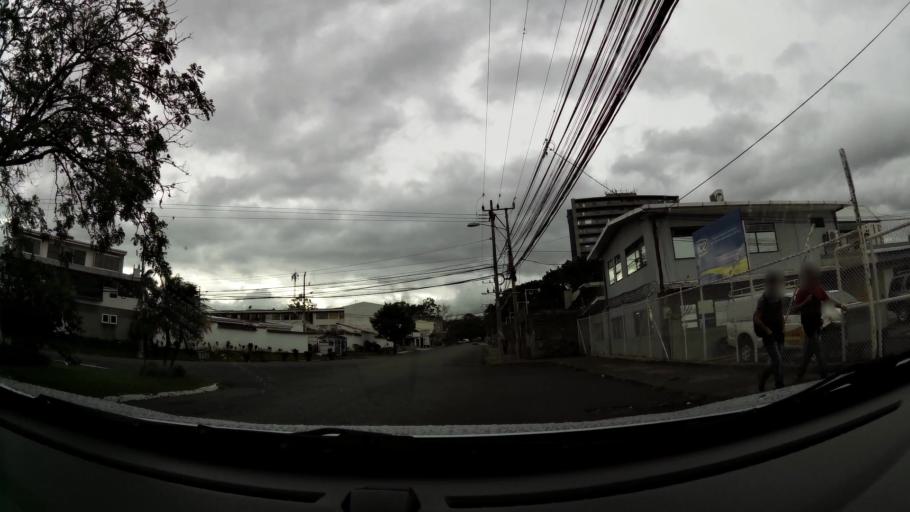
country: CR
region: San Jose
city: Colima
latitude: 9.9406
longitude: -84.1020
